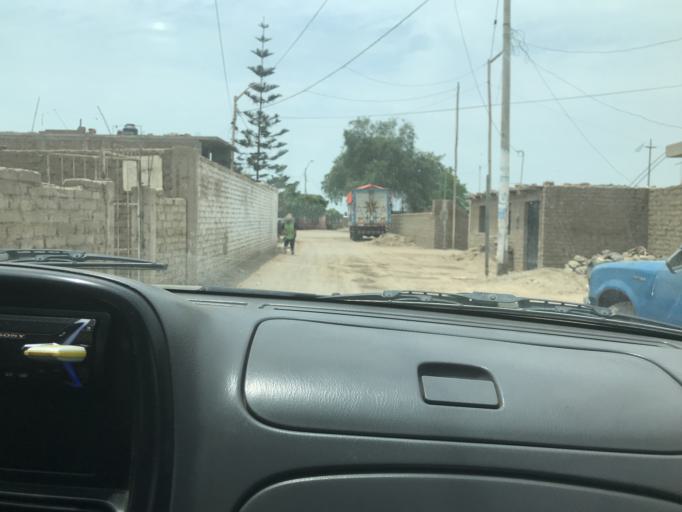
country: PE
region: La Libertad
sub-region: Viru
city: Viru
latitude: -8.4184
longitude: -78.7893
